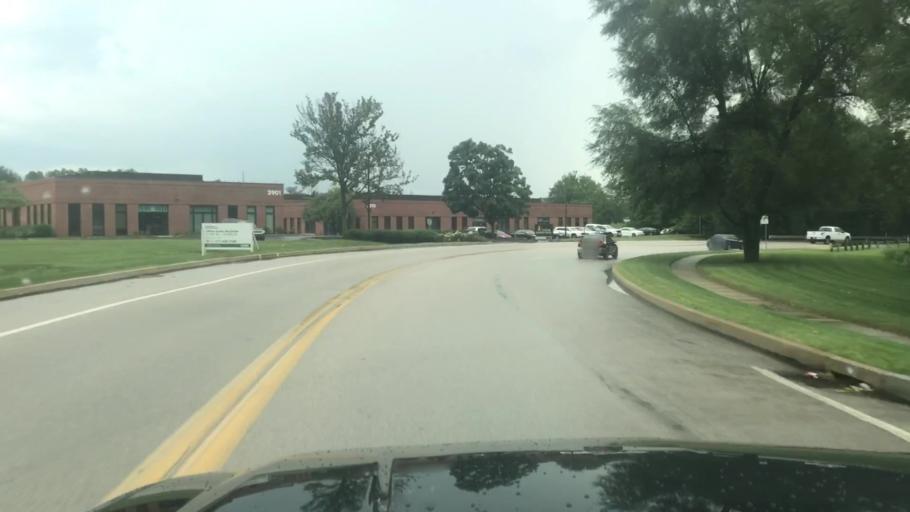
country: US
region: Pennsylvania
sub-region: Cumberland County
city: Shiremanstown
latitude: 40.2130
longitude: -76.9439
